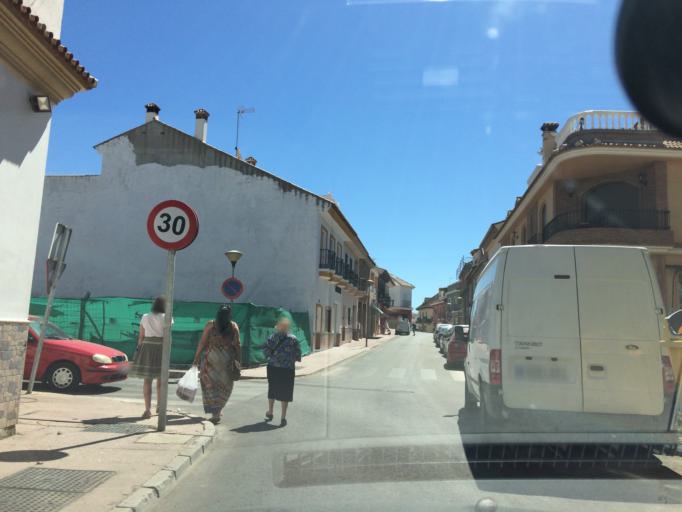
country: ES
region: Andalusia
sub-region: Provincia de Malaga
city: Estacion de Cartama
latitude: 36.7367
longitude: -4.6127
